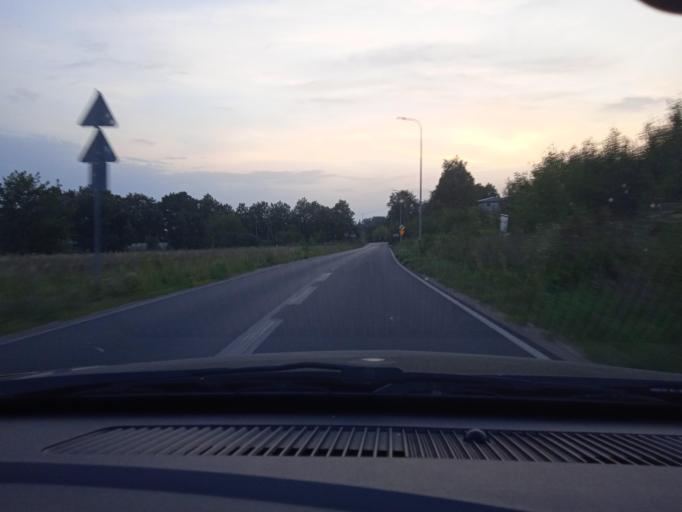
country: PL
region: Masovian Voivodeship
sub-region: Powiat nowodworski
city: Pomiechowek
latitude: 52.4651
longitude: 20.7002
